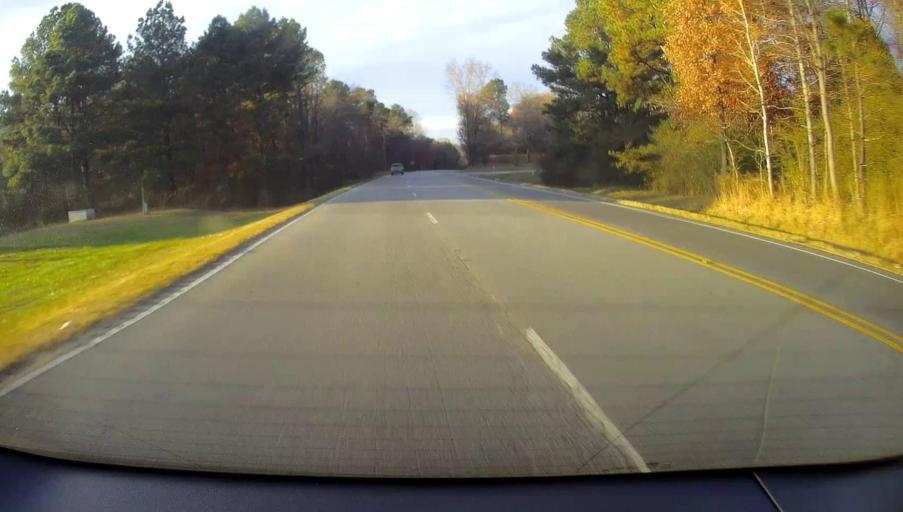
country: US
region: Alabama
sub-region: Blount County
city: Blountsville
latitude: 34.1450
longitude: -86.4500
